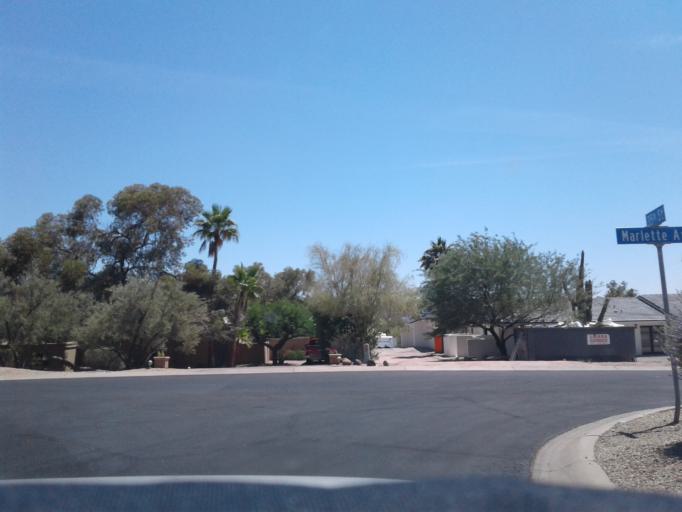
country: US
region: Arizona
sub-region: Maricopa County
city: Paradise Valley
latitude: 33.5305
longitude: -112.0070
